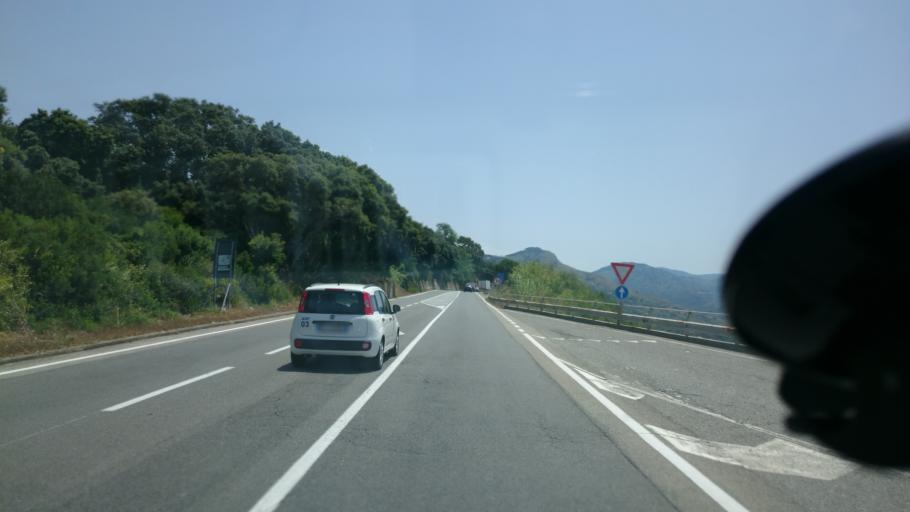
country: IT
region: Calabria
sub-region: Provincia di Cosenza
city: Cittadella del Capo
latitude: 39.5393
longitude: 15.8976
